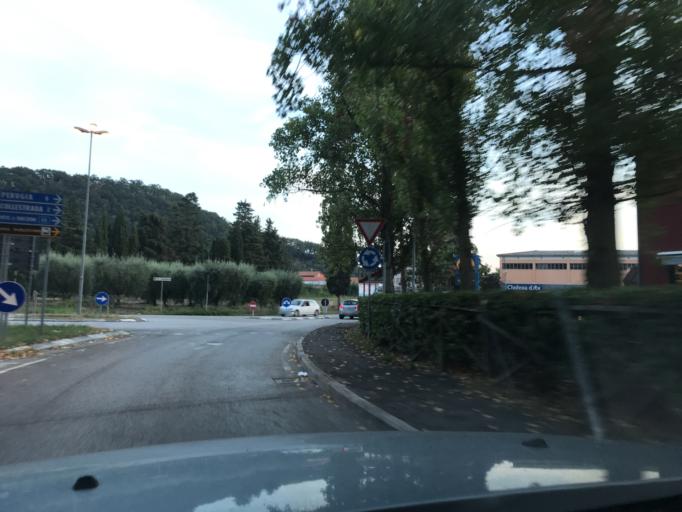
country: IT
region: Umbria
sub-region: Provincia di Perugia
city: Via Lippia
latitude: 43.0905
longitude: 12.4505
